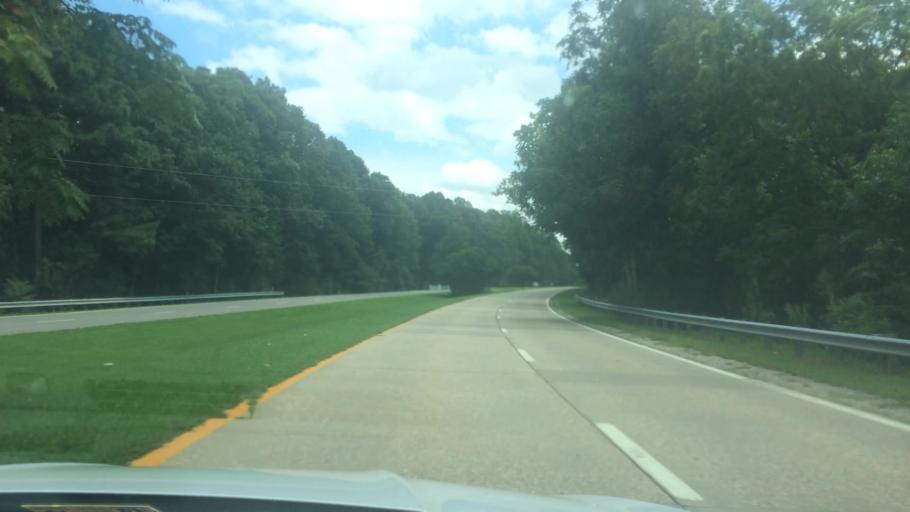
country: US
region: Virginia
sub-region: King William County
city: West Point
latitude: 37.4107
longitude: -76.8604
